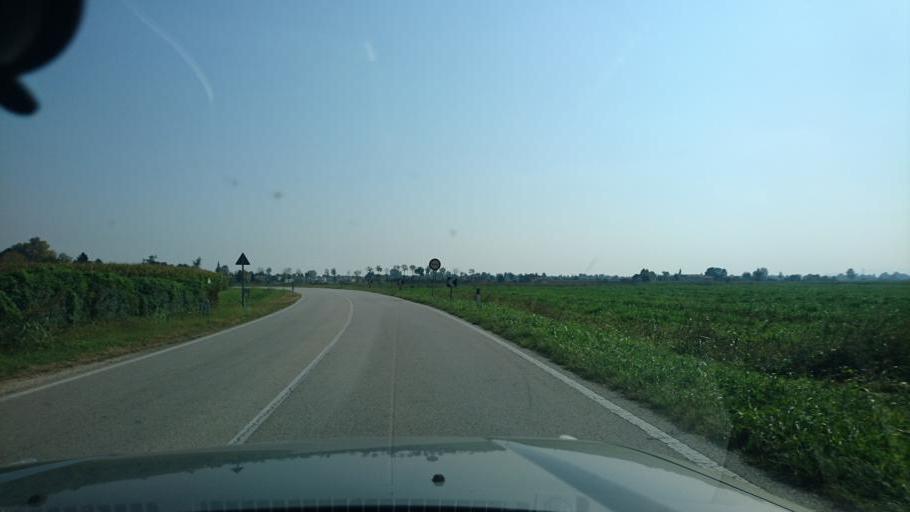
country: IT
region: Veneto
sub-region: Provincia di Vicenza
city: Camisano Vicentino
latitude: 45.5161
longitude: 11.7308
